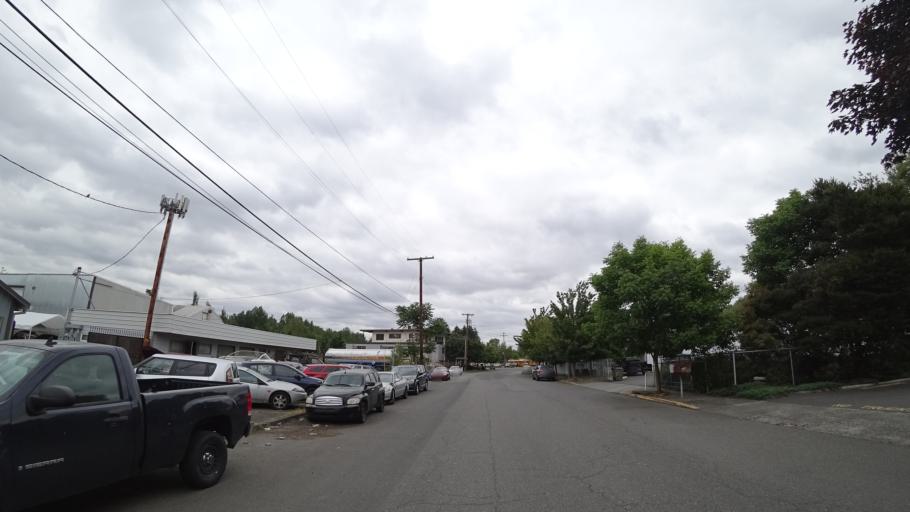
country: US
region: Washington
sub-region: Clark County
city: Vancouver
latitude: 45.5960
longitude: -122.6638
